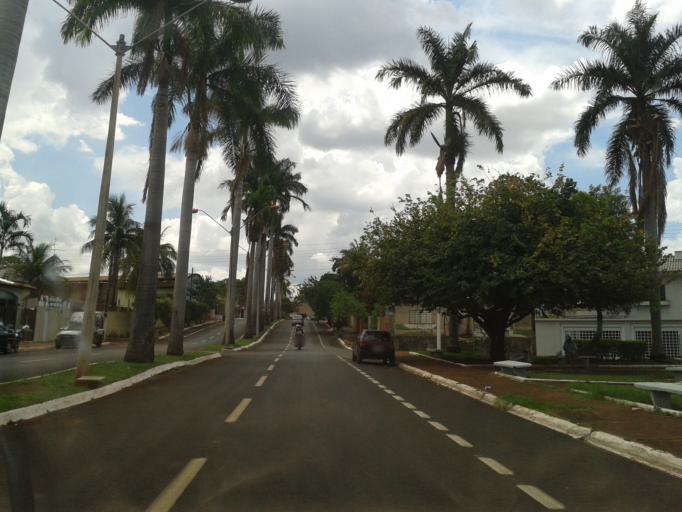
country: BR
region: Goias
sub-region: Itumbiara
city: Itumbiara
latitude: -18.4114
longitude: -49.2105
